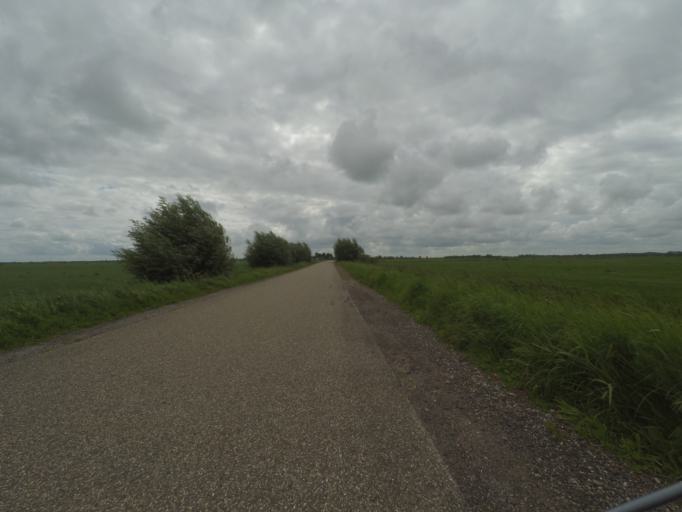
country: NL
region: Friesland
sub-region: Gemeente Kollumerland en Nieuwkruisland
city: Kollumerzwaag
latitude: 53.3139
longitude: 6.0896
